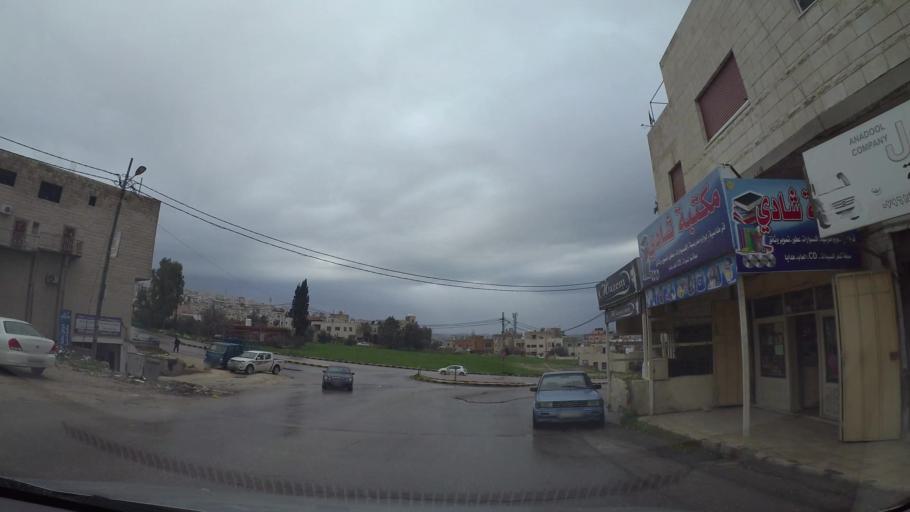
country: JO
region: Amman
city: Al Jubayhah
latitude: 32.0377
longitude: 35.8341
